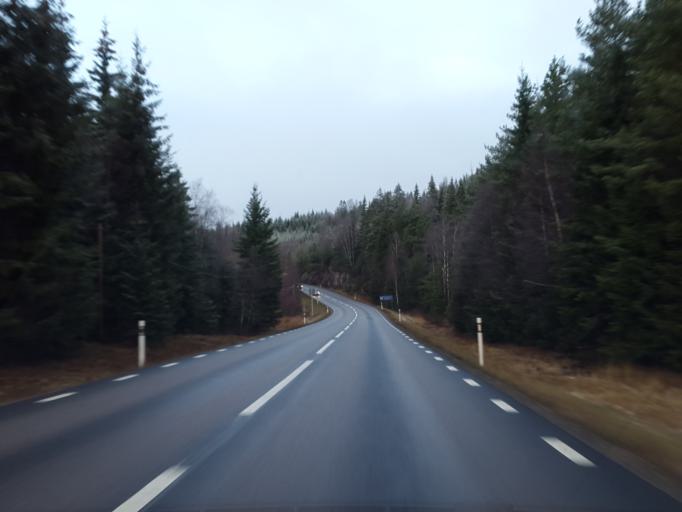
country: SE
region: Vaestra Goetaland
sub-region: Boras Kommun
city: Sandared
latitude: 57.8206
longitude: 12.7377
